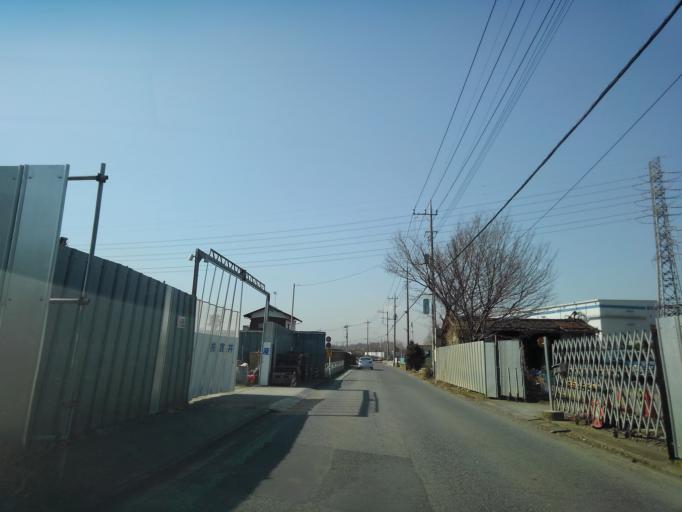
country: JP
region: Saitama
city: Tokorozawa
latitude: 35.7967
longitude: 139.4998
